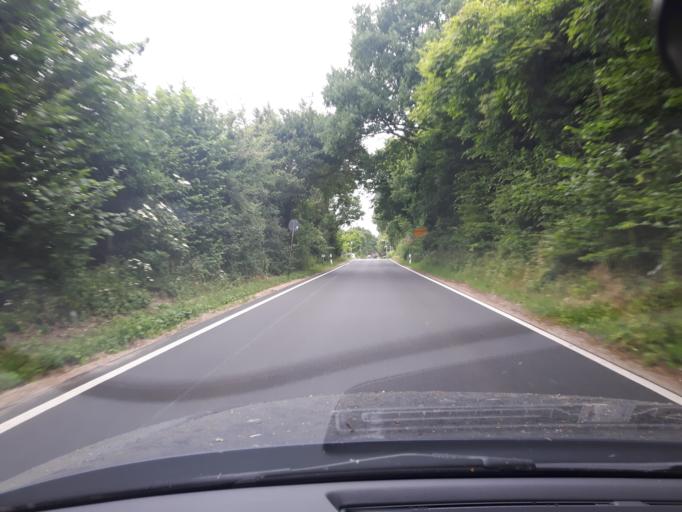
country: DE
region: Schleswig-Holstein
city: Ratekau
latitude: 53.9319
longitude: 10.7841
